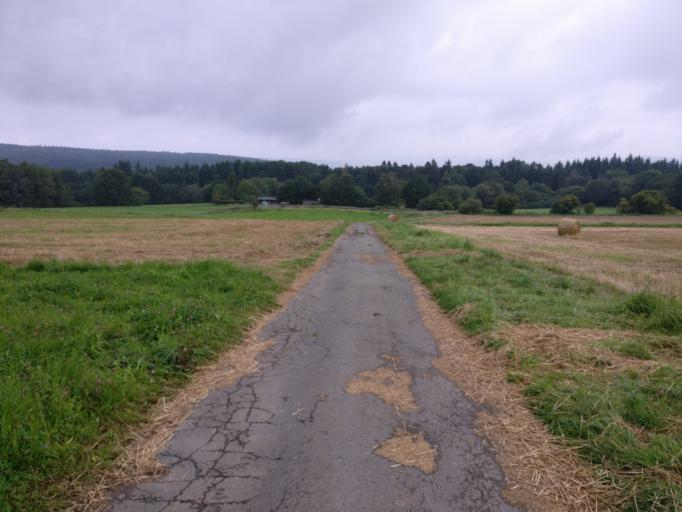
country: DE
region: Hesse
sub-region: Regierungsbezirk Giessen
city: Greifenstein
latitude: 50.6250
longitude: 8.2803
